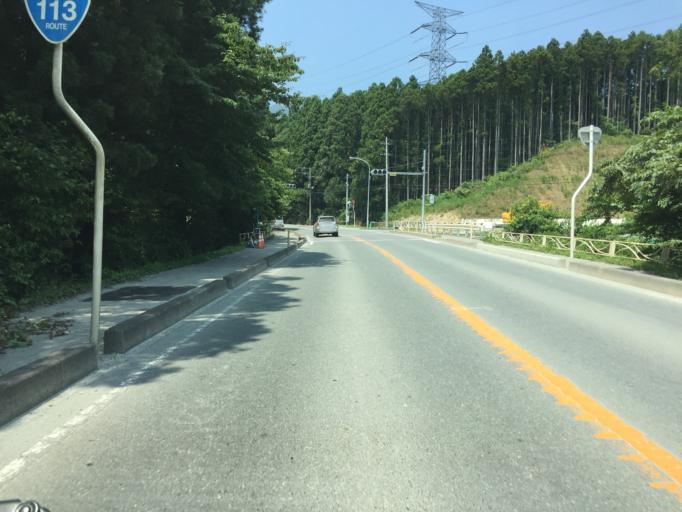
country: JP
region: Miyagi
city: Marumori
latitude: 37.8515
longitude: 140.8768
